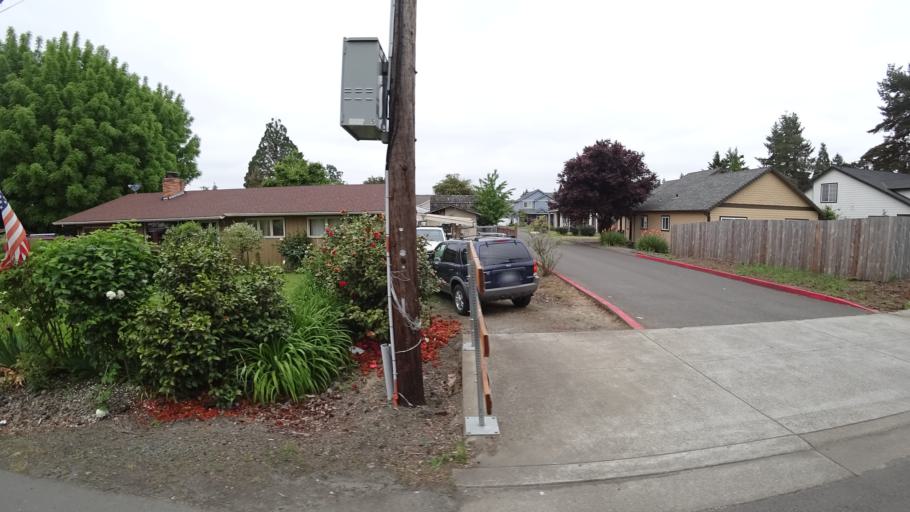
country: US
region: Oregon
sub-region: Washington County
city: Aloha
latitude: 45.5008
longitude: -122.9116
